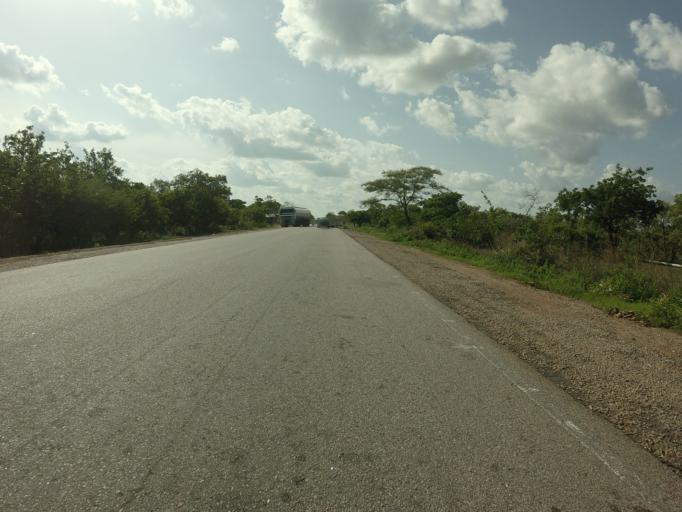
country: GH
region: Upper East
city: Bolgatanga
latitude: 10.5234
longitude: -0.8142
